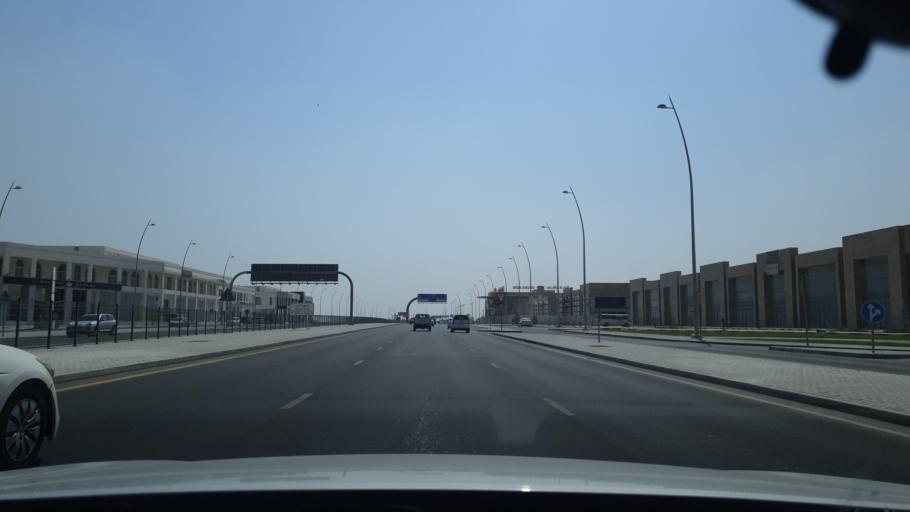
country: QA
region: Al Khawr
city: Al Khawr
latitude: 25.6696
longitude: 51.5009
